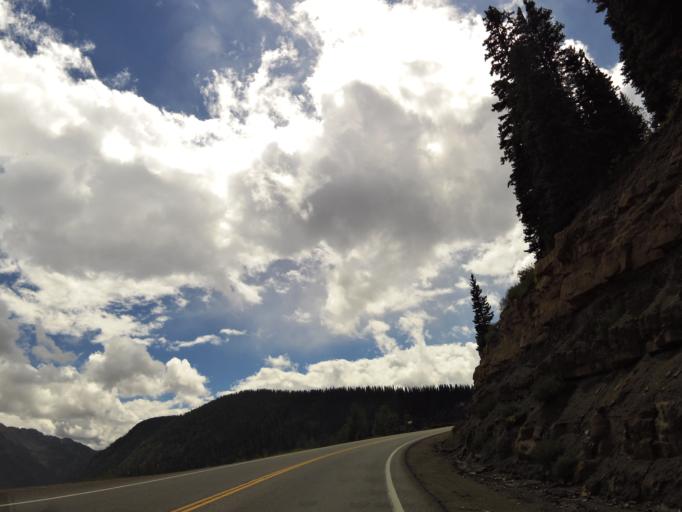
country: US
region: Colorado
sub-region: San Juan County
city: Silverton
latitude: 37.7025
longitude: -107.7682
